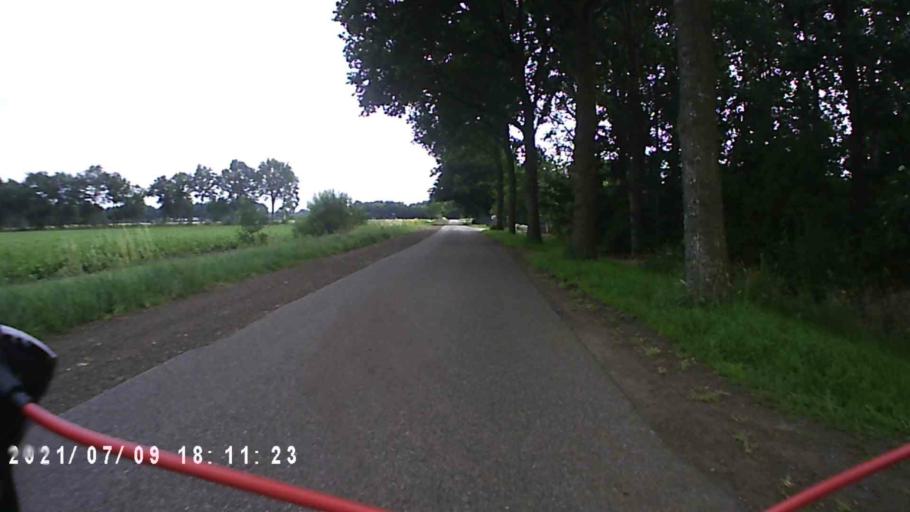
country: NL
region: Groningen
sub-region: Gemeente Pekela
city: Oude Pekela
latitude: 53.0684
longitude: 7.0325
